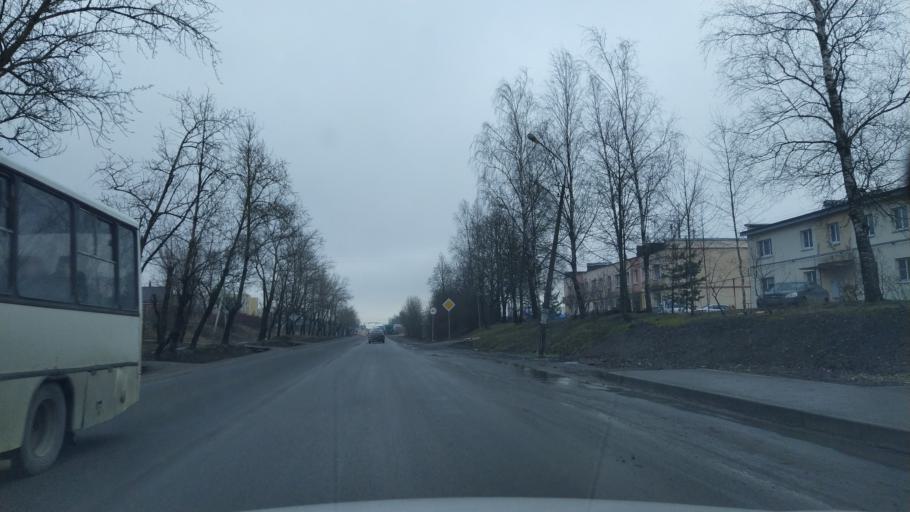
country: RU
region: St.-Petersburg
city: Aleksandrovskaya
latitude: 59.7239
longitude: 30.2566
